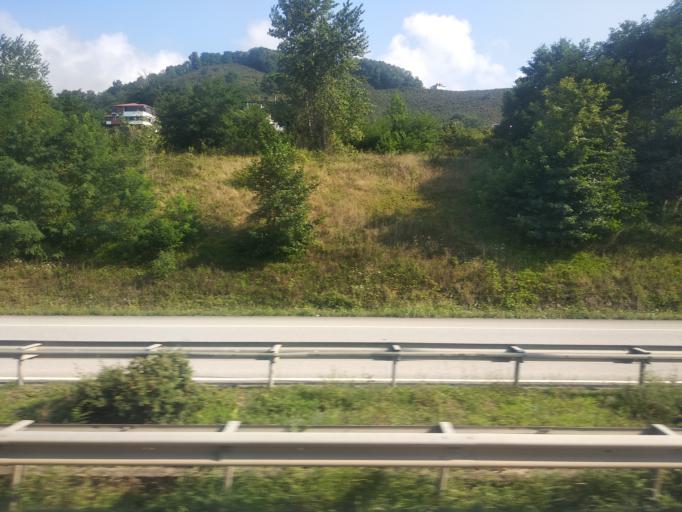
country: TR
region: Ordu
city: Ordu
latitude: 41.0136
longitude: 37.8369
